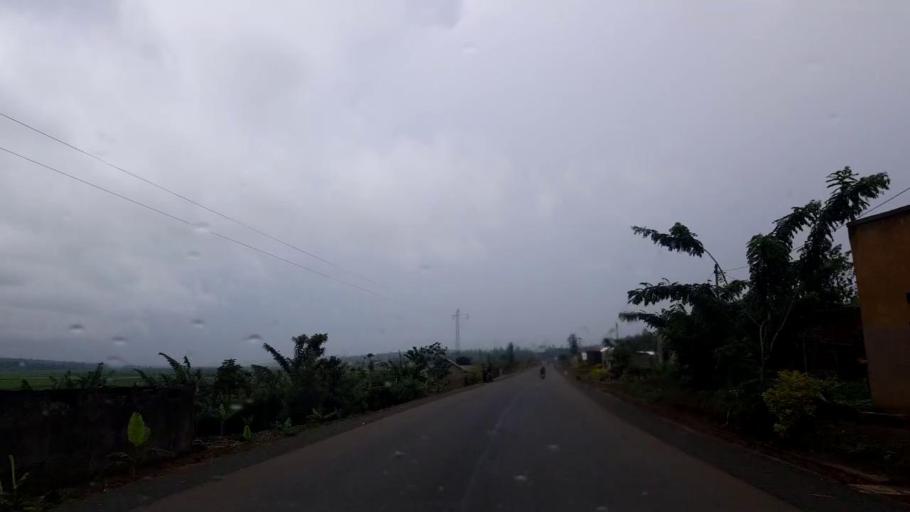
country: RW
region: Northern Province
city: Byumba
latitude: -1.4185
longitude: 30.2784
